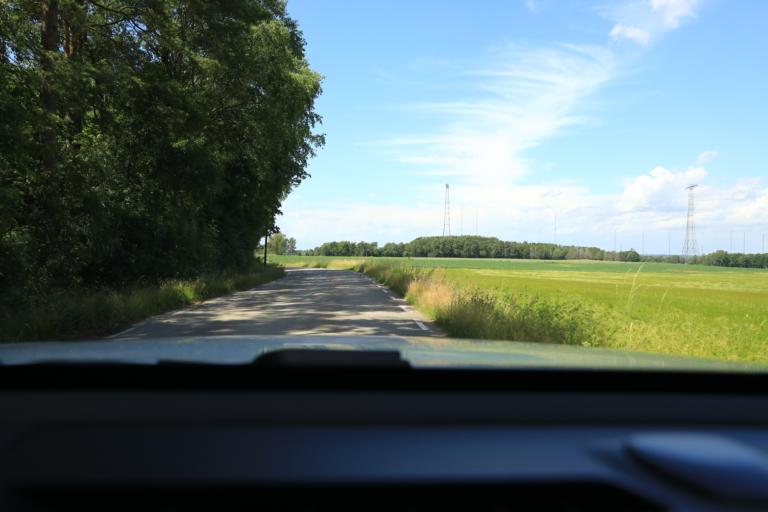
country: SE
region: Halland
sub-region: Varbergs Kommun
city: Tvaaker
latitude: 57.0955
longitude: 12.3927
